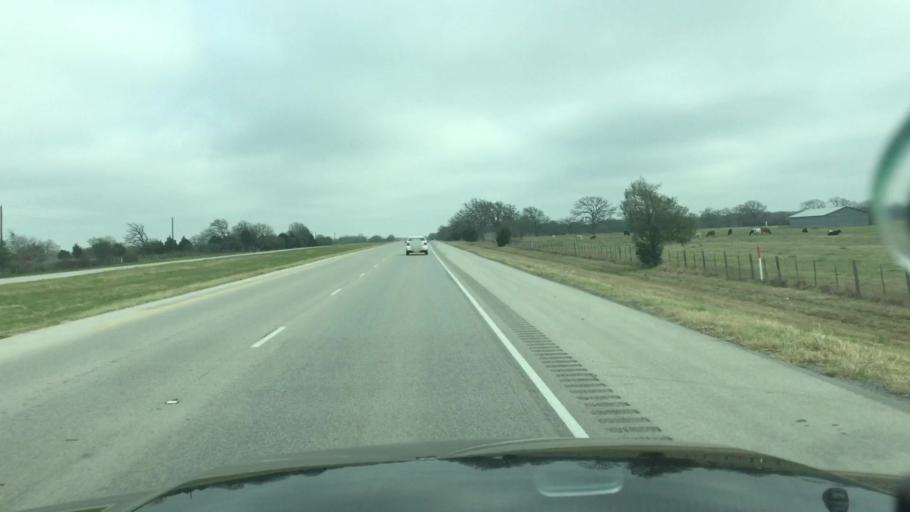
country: US
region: Texas
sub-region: Lee County
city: Giddings
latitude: 30.1446
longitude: -96.7276
